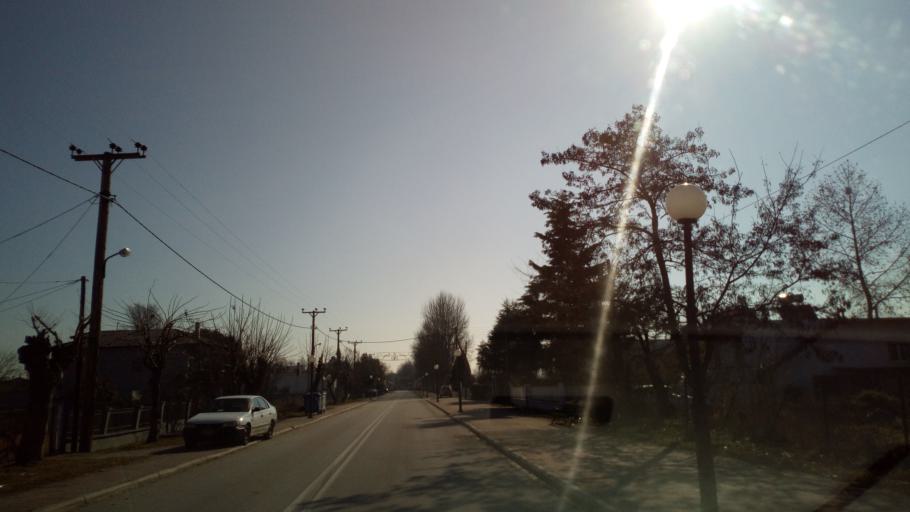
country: GR
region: Central Macedonia
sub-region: Nomos Thessalonikis
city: Lagkadas
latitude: 40.7437
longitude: 23.0759
